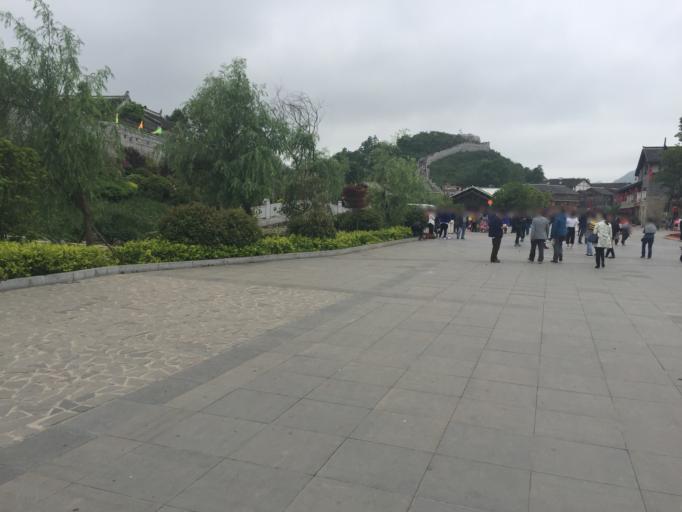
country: CN
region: Guizhou Sheng
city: Guiyang
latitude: 26.3377
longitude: 106.6845
